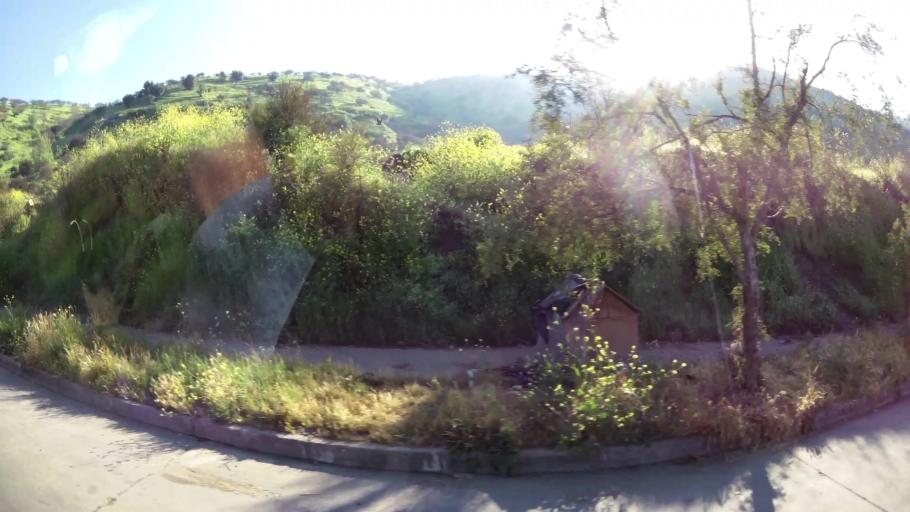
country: CL
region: Santiago Metropolitan
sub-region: Provincia de Chacabuco
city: Chicureo Abajo
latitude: -33.3693
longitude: -70.6496
